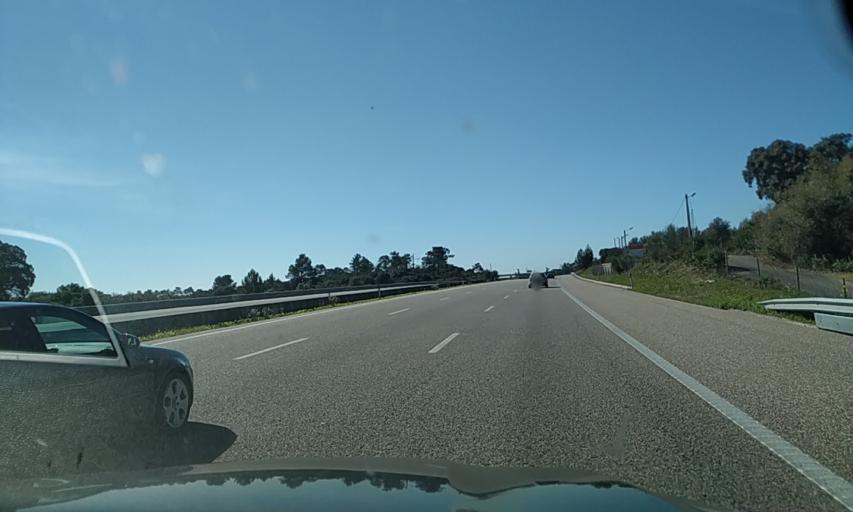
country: PT
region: Santarem
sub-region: Alcanena
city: Alcanena
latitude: 39.4299
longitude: -8.6289
